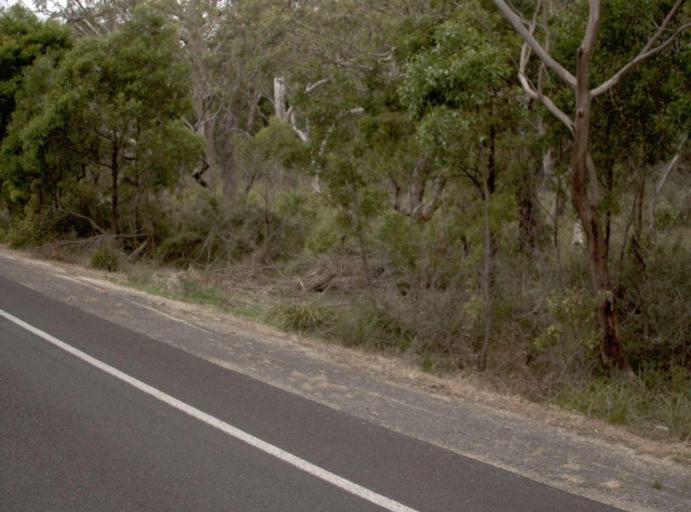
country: AU
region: Victoria
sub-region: Wellington
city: Sale
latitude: -38.2158
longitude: 147.0613
